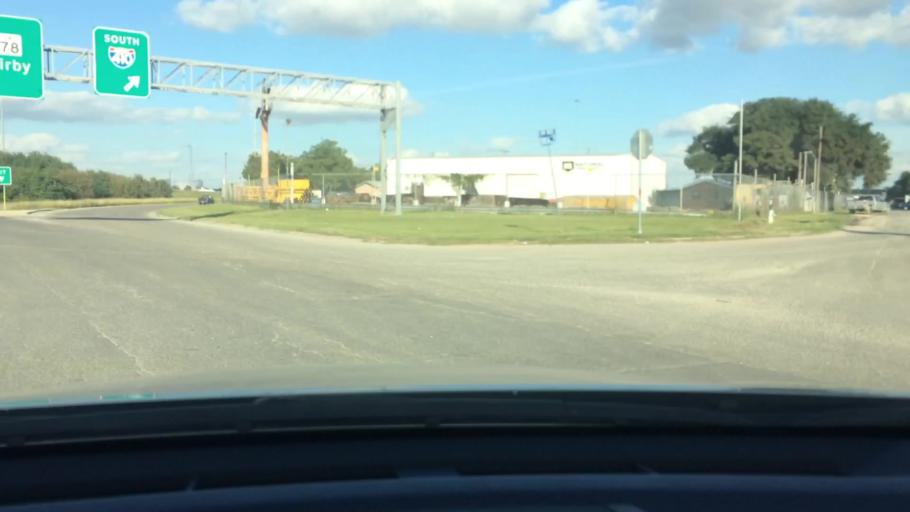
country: US
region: Texas
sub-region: Bexar County
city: Kirby
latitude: 29.4458
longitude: -98.4044
